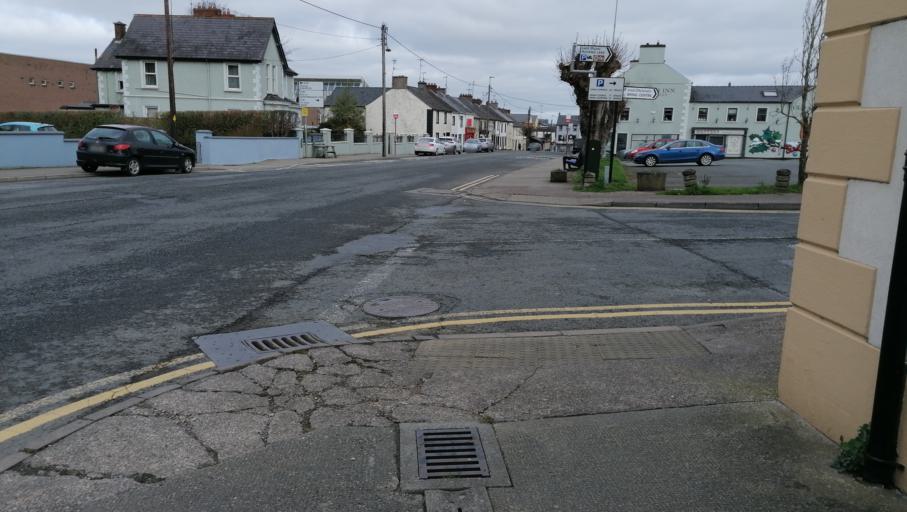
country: IE
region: Ulster
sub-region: County Monaghan
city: Castleblayney
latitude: 54.1184
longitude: -6.7364
